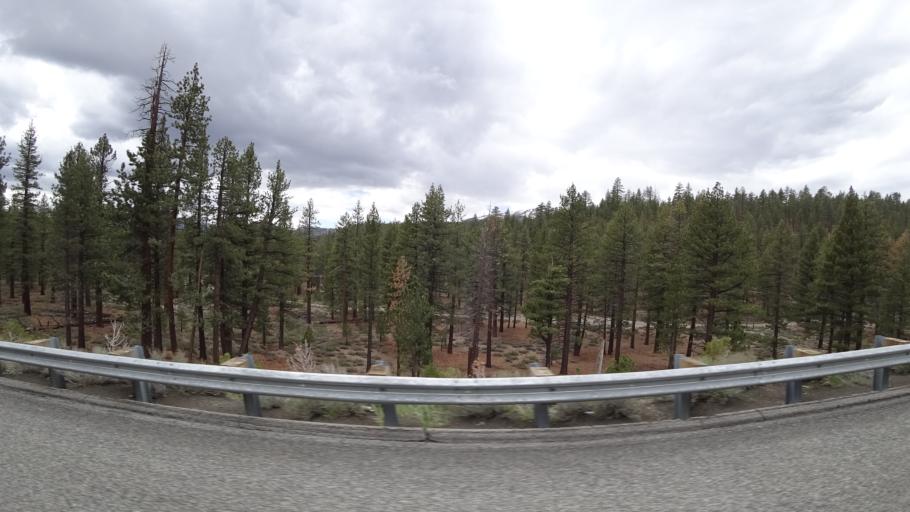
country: US
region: California
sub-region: Mono County
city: Mammoth Lakes
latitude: 37.7570
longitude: -118.9873
